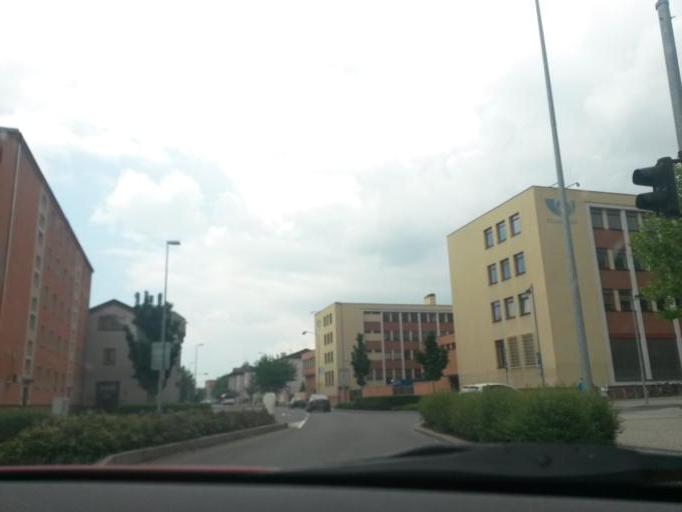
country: CZ
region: Olomoucky
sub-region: Okres Olomouc
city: Olomouc
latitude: 49.5931
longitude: 17.2768
